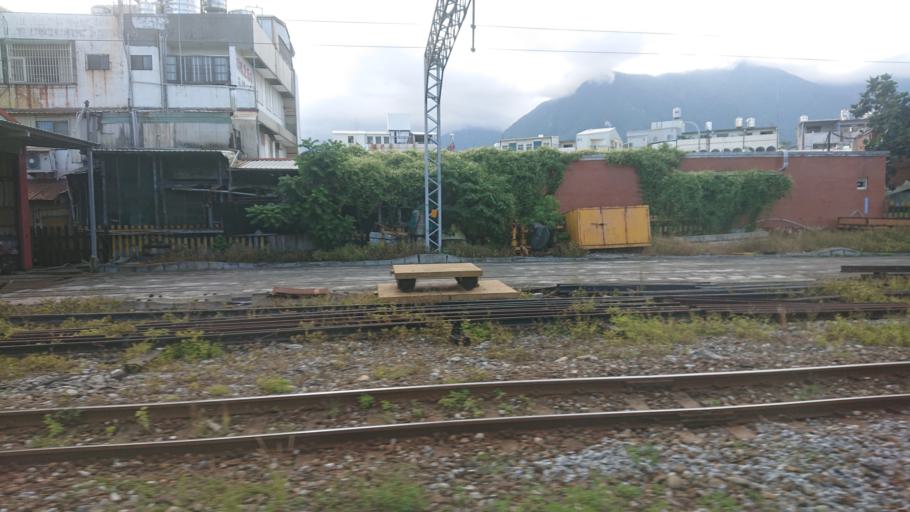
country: TW
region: Taiwan
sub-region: Hualien
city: Hualian
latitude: 23.9894
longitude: 121.5992
